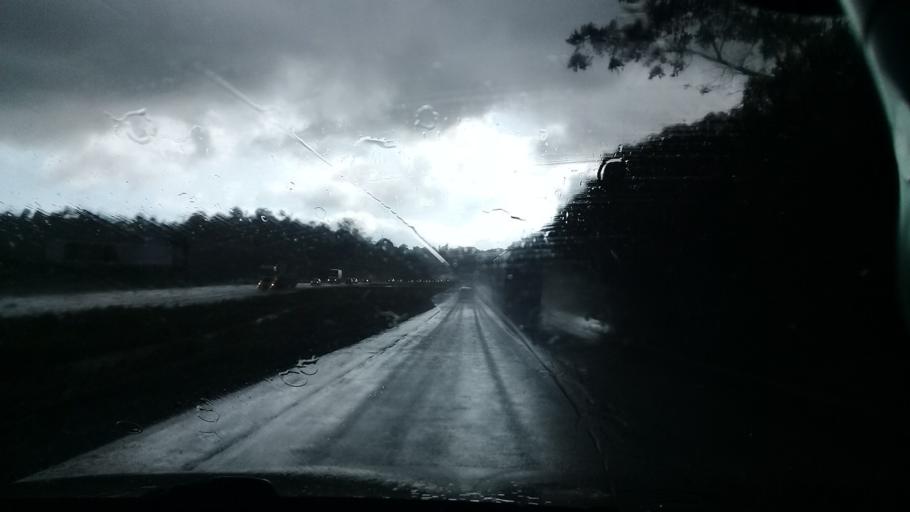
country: BR
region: Pernambuco
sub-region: Moreno
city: Moreno
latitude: -8.1108
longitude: -35.1485
